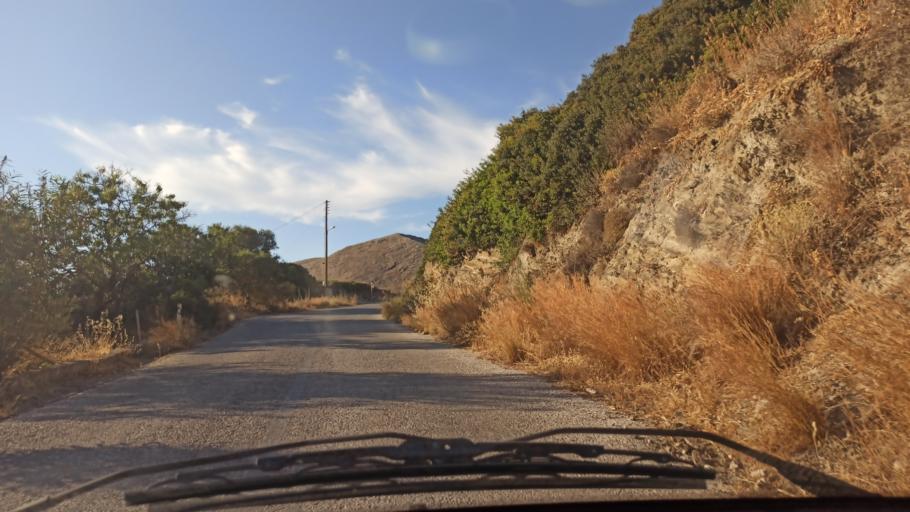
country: GR
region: South Aegean
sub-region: Nomos Kykladon
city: Ano Syros
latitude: 37.4433
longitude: 24.9160
